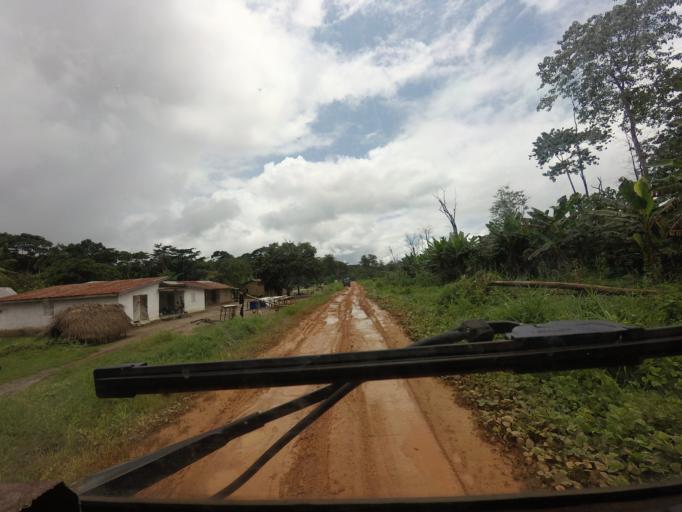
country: SL
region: Eastern Province
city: Tombodu
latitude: 8.1354
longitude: -10.6549
